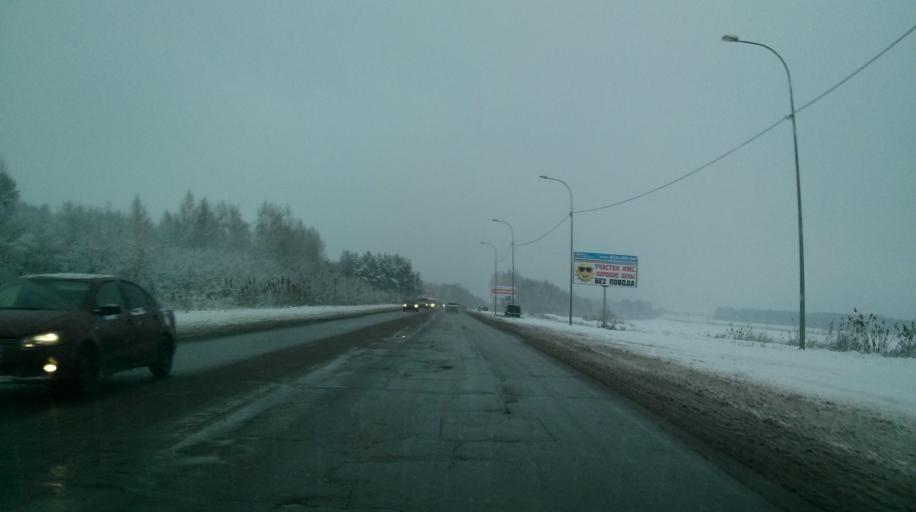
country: RU
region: Nizjnij Novgorod
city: Burevestnik
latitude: 56.1674
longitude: 43.7329
